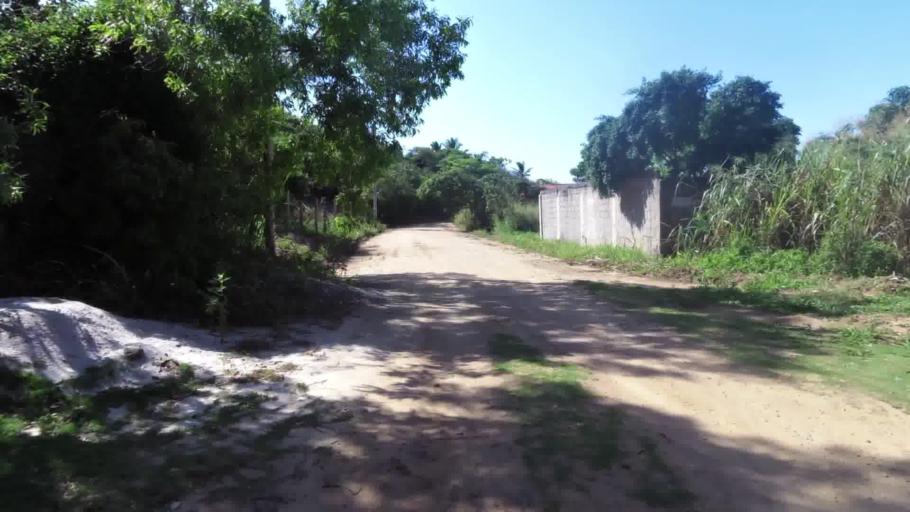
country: BR
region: Espirito Santo
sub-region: Piuma
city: Piuma
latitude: -20.8217
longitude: -40.6166
